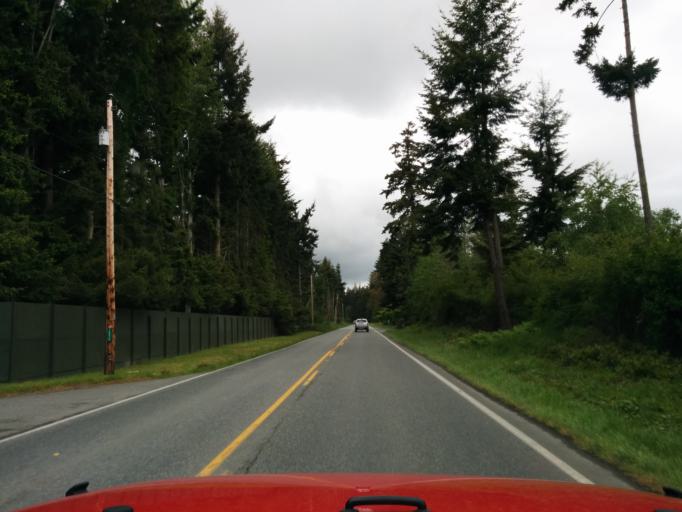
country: US
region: Washington
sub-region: Island County
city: Coupeville
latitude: 48.1765
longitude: -122.6175
